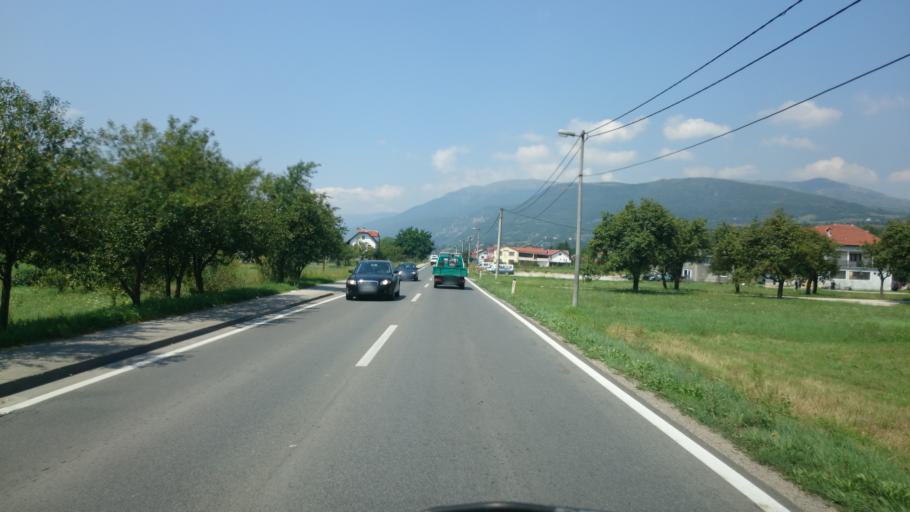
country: BA
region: Federation of Bosnia and Herzegovina
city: Travnik
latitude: 44.2027
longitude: 17.7229
